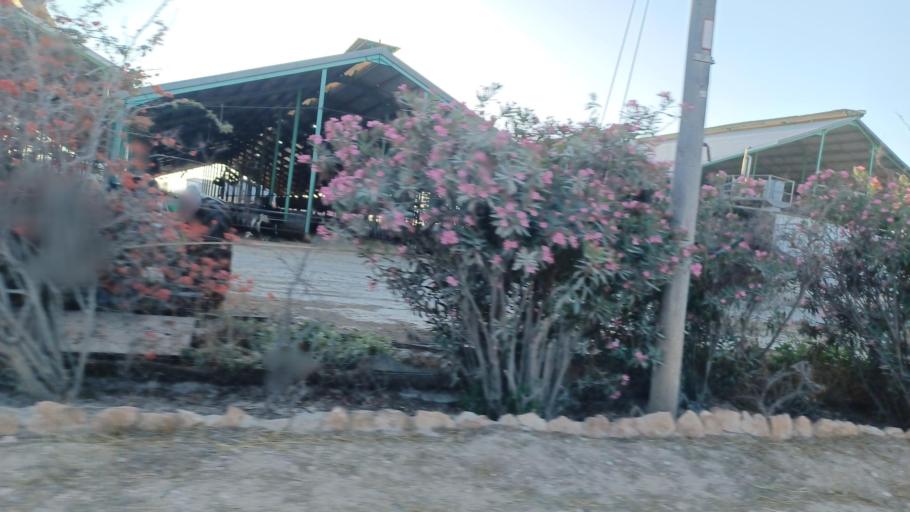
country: CY
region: Ammochostos
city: Achna
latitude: 35.0170
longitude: 33.8003
